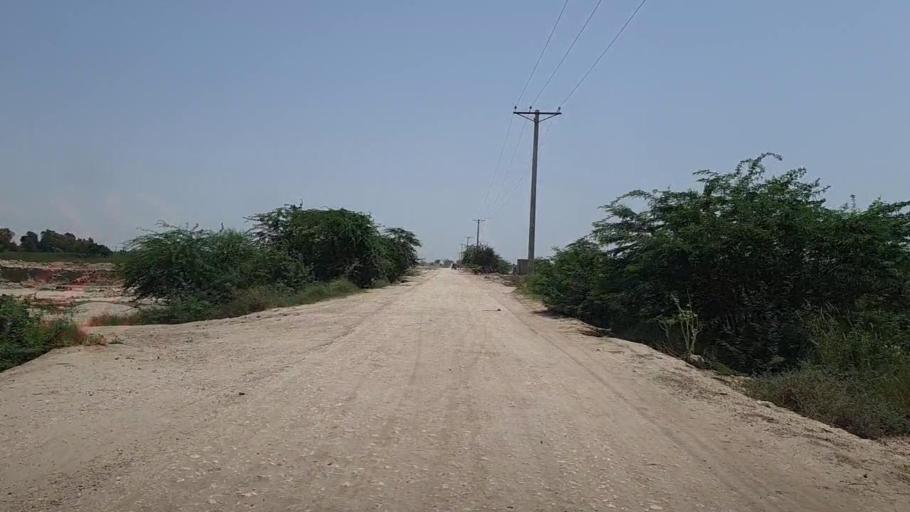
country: PK
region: Sindh
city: Pad Idan
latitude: 26.7704
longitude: 68.2920
